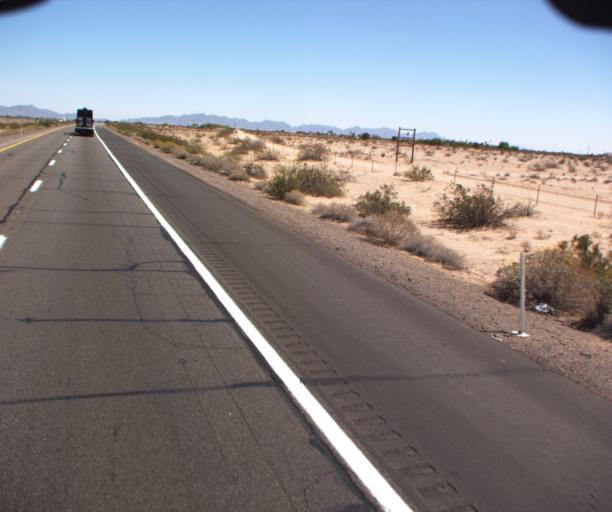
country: US
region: Arizona
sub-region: Yuma County
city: Wellton
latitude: 32.6861
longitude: -113.9993
